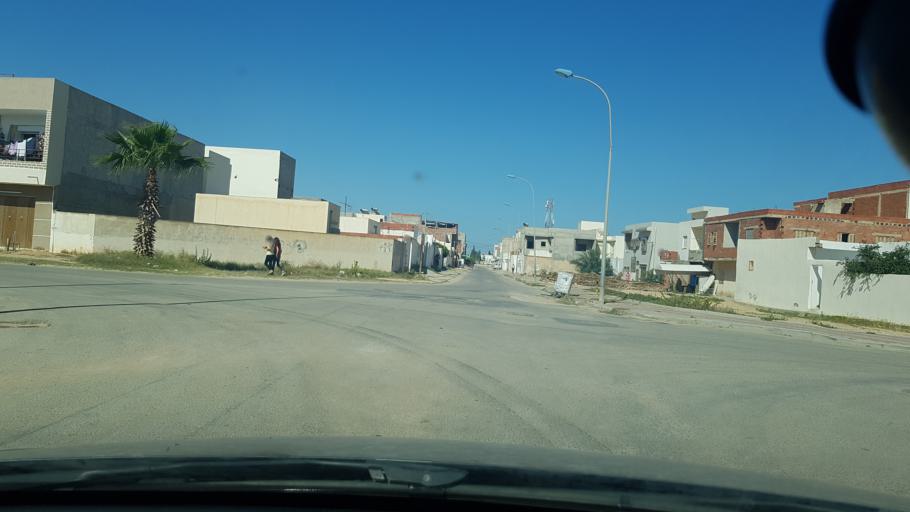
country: TN
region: Safaqis
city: Al Qarmadah
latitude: 34.8253
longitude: 10.7530
